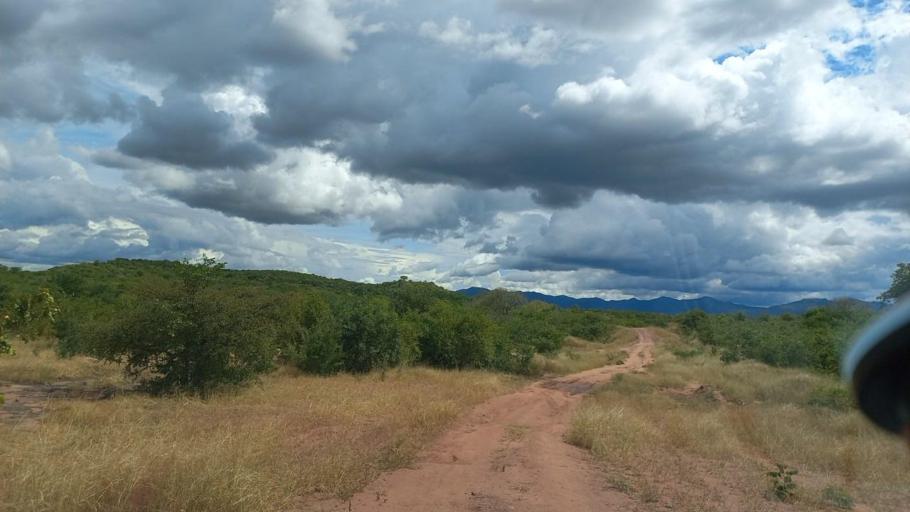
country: ZM
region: Lusaka
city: Luangwa
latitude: -15.6277
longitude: 30.3909
